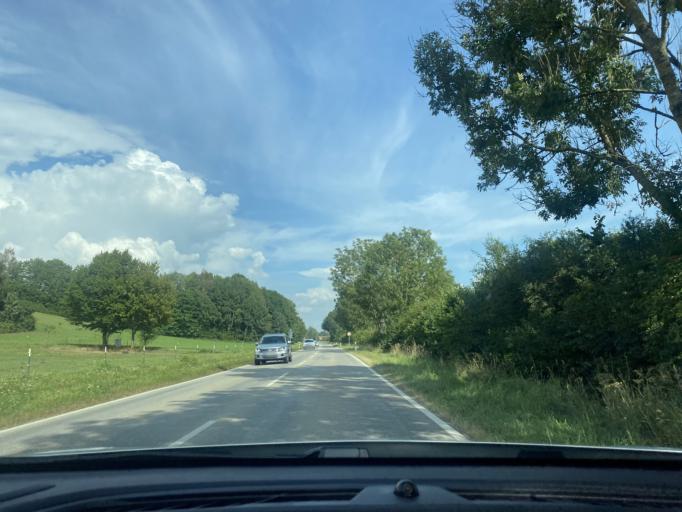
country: DE
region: Bavaria
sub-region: Upper Bavaria
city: Haag an der Amper
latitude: 48.4578
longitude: 11.8152
